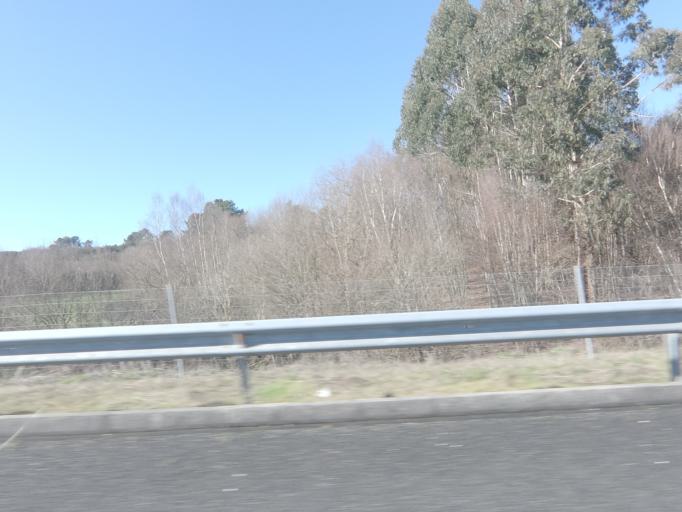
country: ES
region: Galicia
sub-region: Provincia de Pontevedra
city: Lalin
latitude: 42.6550
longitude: -8.1397
